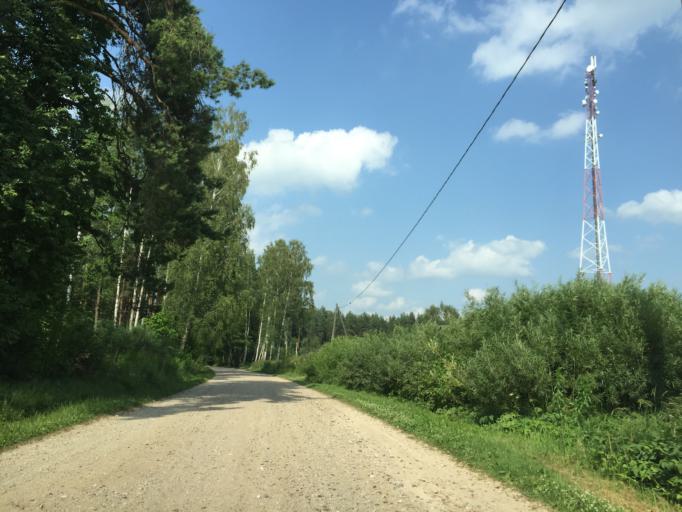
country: LV
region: Ozolnieku
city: Ozolnieki
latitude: 56.6732
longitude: 23.7568
